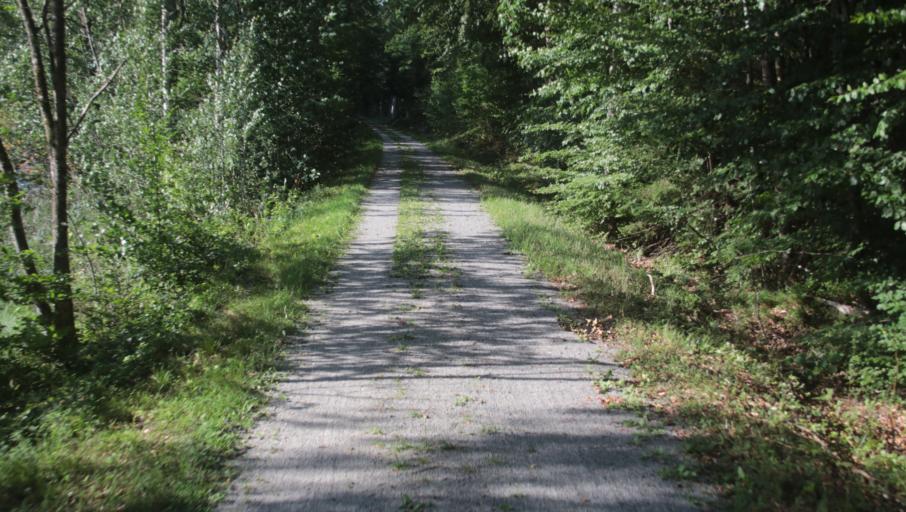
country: SE
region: Blekinge
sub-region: Karlshamns Kommun
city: Svangsta
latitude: 56.3574
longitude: 14.6910
